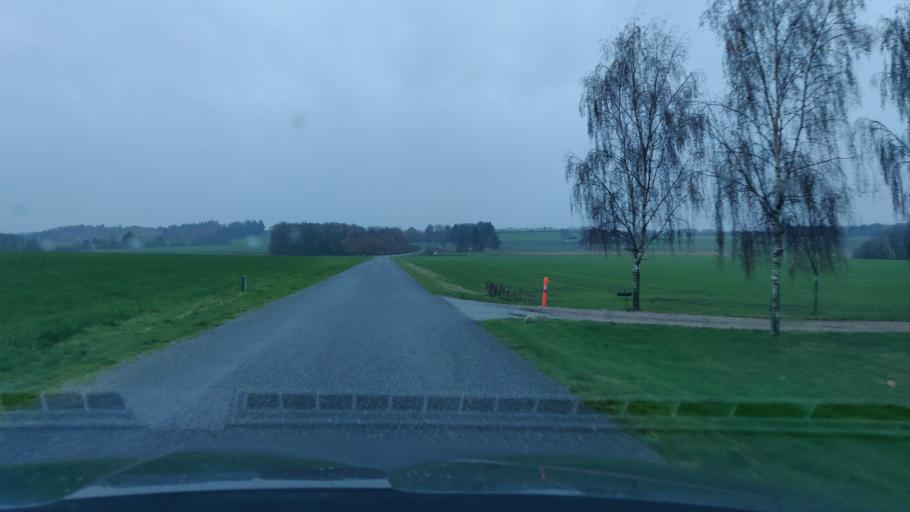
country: DK
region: Central Jutland
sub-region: Herning Kommune
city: Avlum
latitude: 56.2450
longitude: 8.7948
